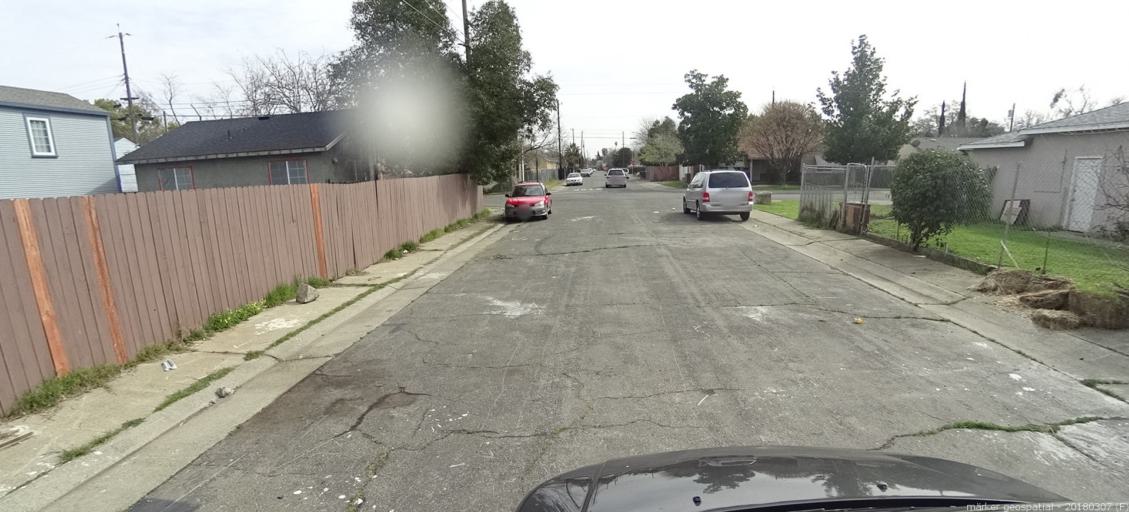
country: US
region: California
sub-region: Sacramento County
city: Parkway
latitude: 38.5359
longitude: -121.4600
